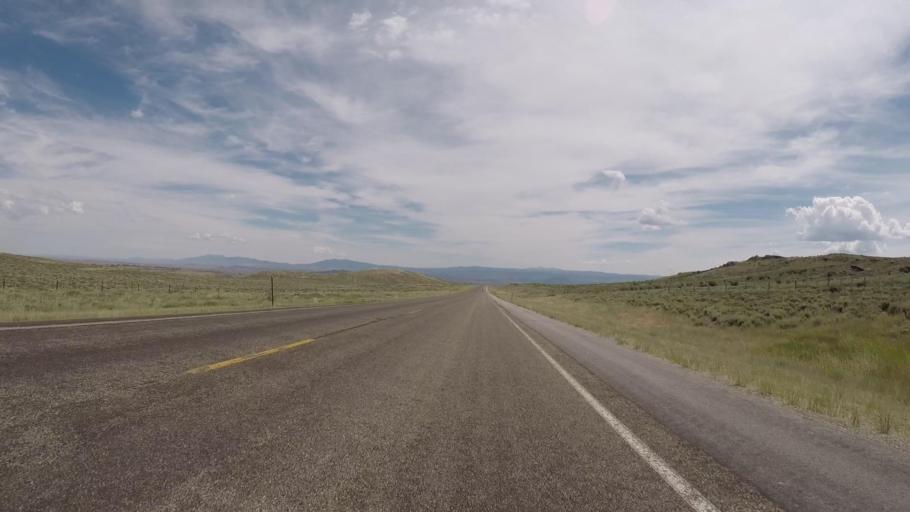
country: US
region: Wyoming
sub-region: Carbon County
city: Saratoga
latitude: 41.1985
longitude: -106.8380
